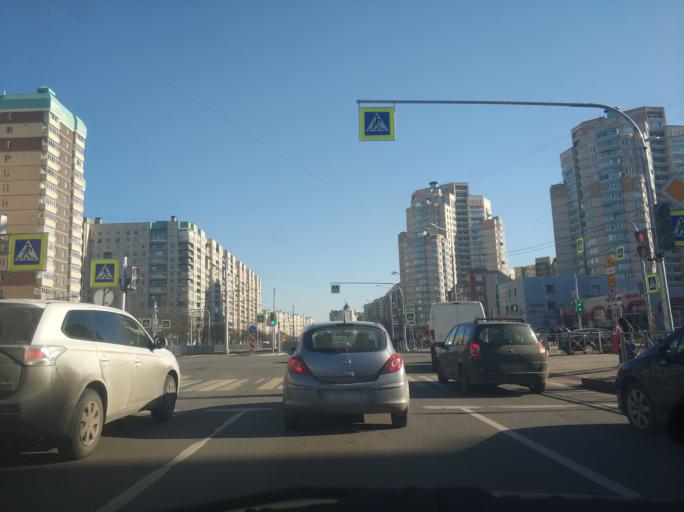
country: RU
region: St.-Petersburg
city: Krasnogvargeisky
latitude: 59.9544
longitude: 30.4822
